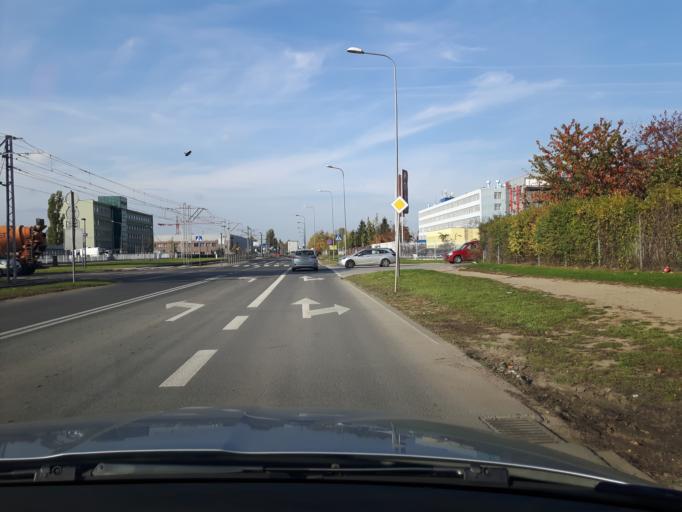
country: PL
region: Masovian Voivodeship
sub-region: Warszawa
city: Targowek
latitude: 52.2999
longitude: 21.0225
